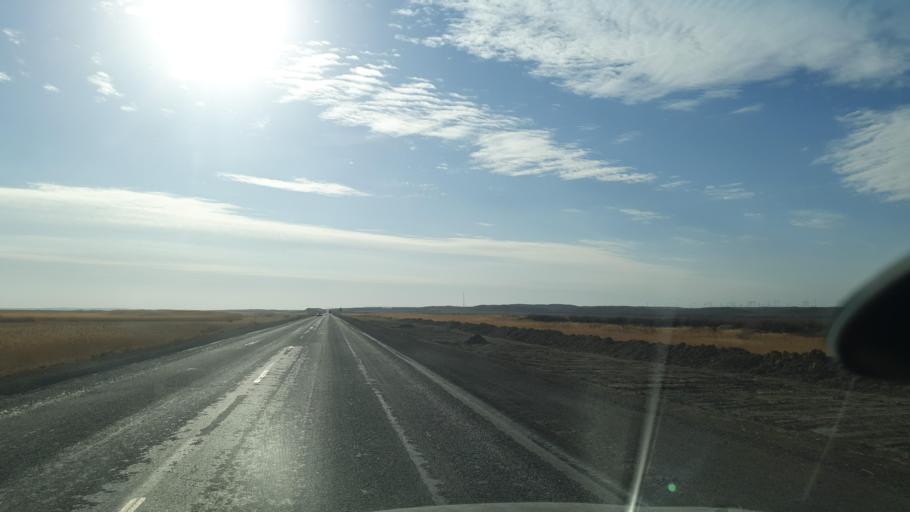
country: KZ
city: Priozersk
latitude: 45.8414
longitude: 73.4577
